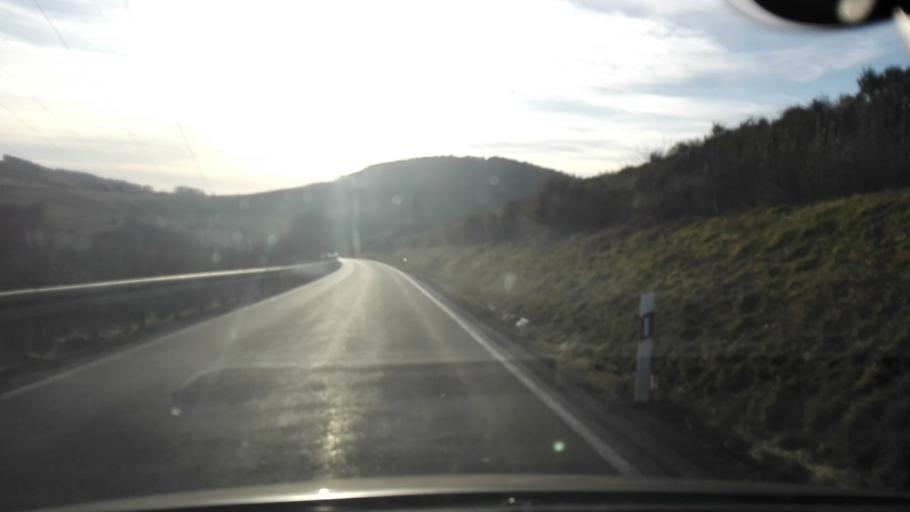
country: DE
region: North Rhine-Westphalia
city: Eslohe
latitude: 51.1703
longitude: 8.1523
